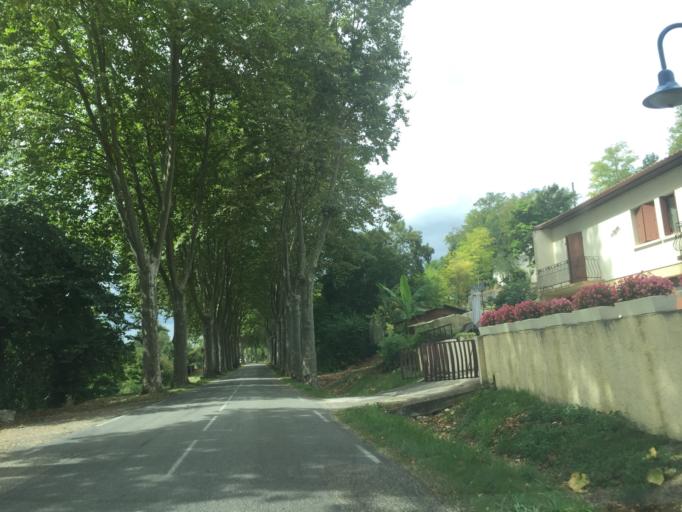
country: FR
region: Midi-Pyrenees
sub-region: Departement du Gers
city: Valence-sur-Baise
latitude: 43.8809
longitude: 0.3798
